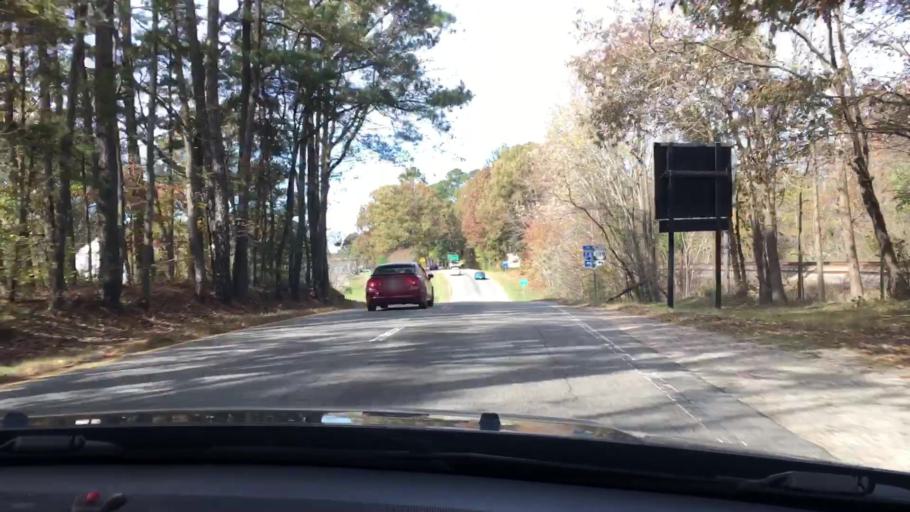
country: US
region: Virginia
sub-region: James City County
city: Williamsburg
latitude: 37.3326
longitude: -76.7453
